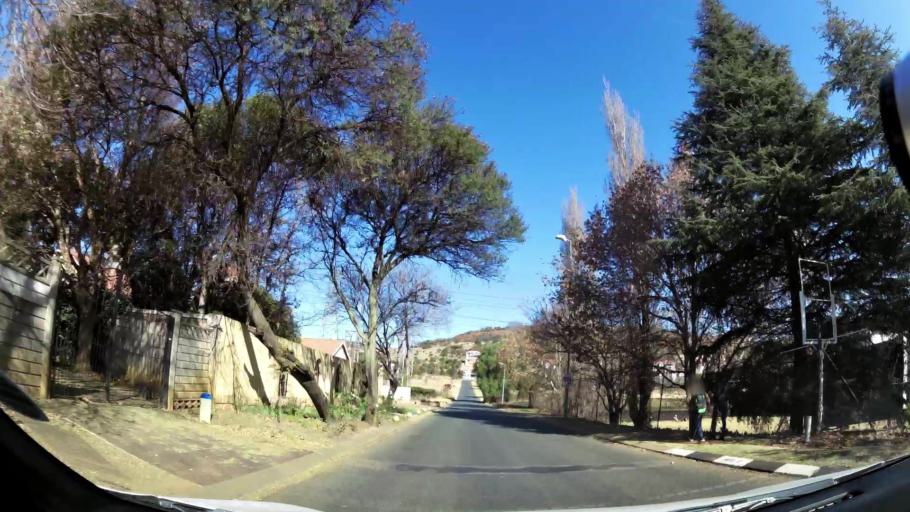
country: ZA
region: Gauteng
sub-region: City of Johannesburg Metropolitan Municipality
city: Johannesburg
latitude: -26.2756
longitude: 28.0239
